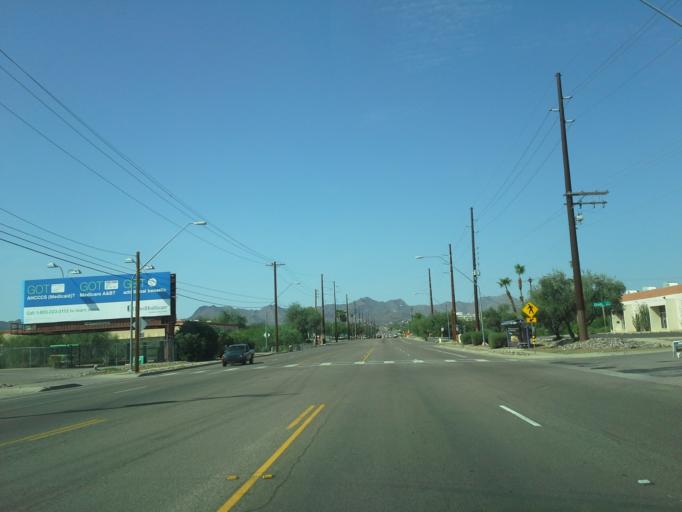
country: US
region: Arizona
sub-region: Pima County
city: Flowing Wells
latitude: 32.2506
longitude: -111.0045
